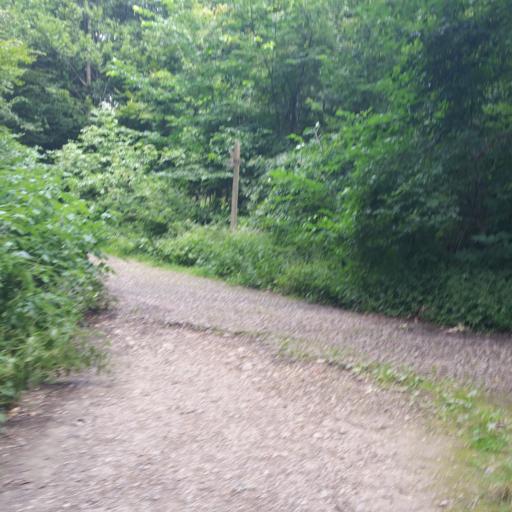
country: AT
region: Vienna
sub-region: Wien Stadt
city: Vienna
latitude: 48.2183
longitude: 16.2751
